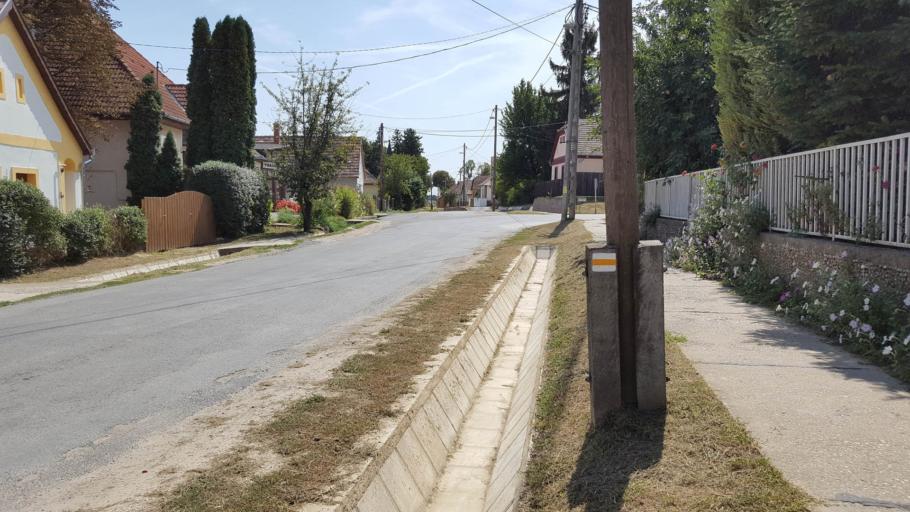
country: HU
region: Somogy
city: Somogyvar
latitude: 46.5711
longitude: 17.6839
